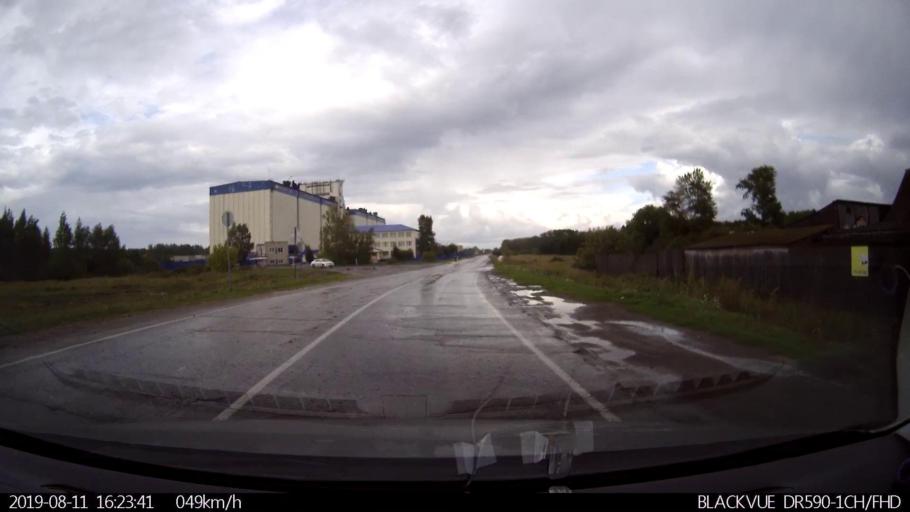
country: RU
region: Ulyanovsk
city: Mayna
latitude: 54.0968
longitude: 47.5889
